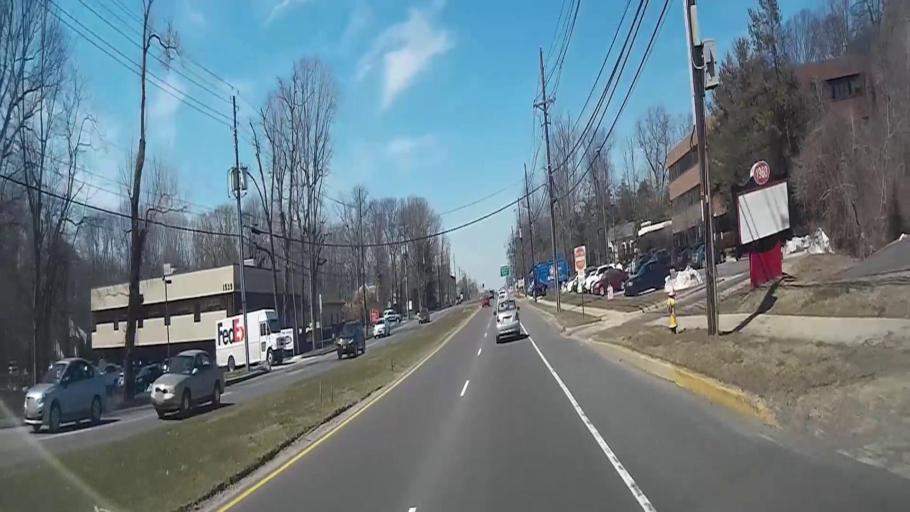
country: US
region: New Jersey
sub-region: Camden County
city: Greentree
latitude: 39.9007
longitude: -74.9604
